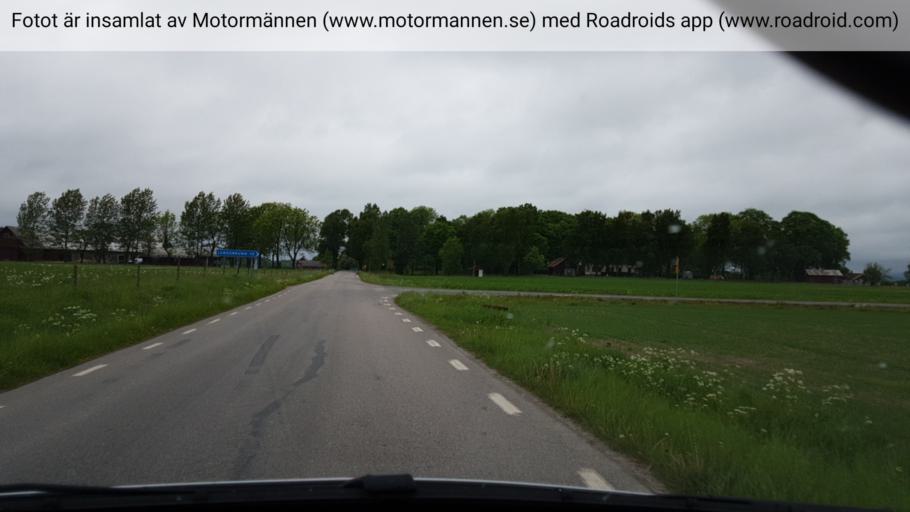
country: SE
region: Vaestra Goetaland
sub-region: Gotene Kommun
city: Kallby
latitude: 58.4616
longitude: 13.3353
